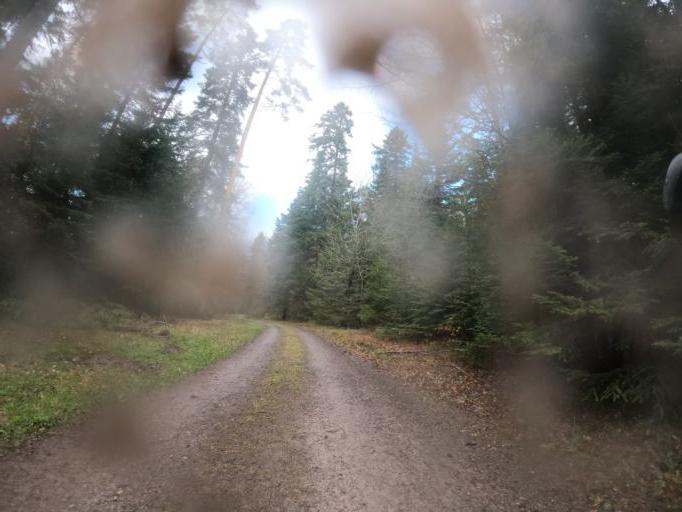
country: DE
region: Baden-Wuerttemberg
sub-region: Karlsruhe Region
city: Neuweiler
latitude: 48.7019
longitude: 8.5831
